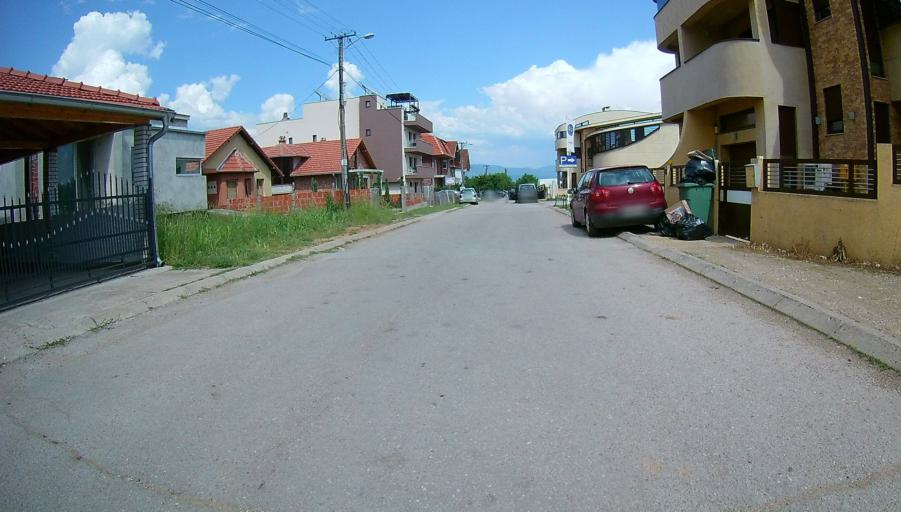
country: RS
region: Central Serbia
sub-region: Nisavski Okrug
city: Nis
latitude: 43.3064
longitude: 21.9147
